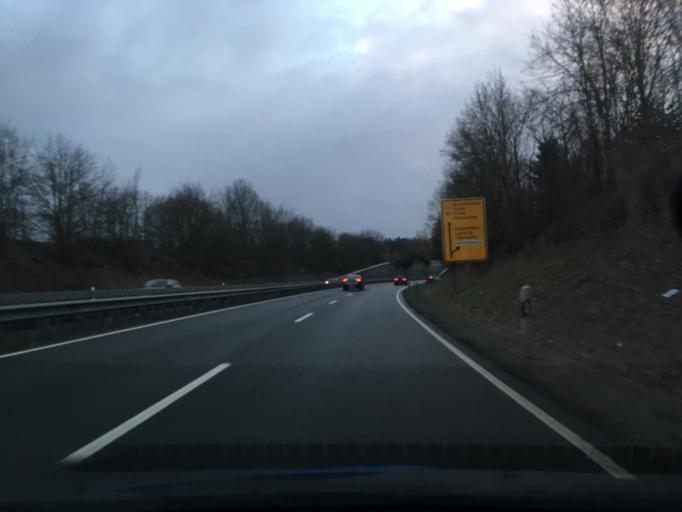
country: DE
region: Lower Saxony
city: Adendorf
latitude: 53.2645
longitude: 10.4420
